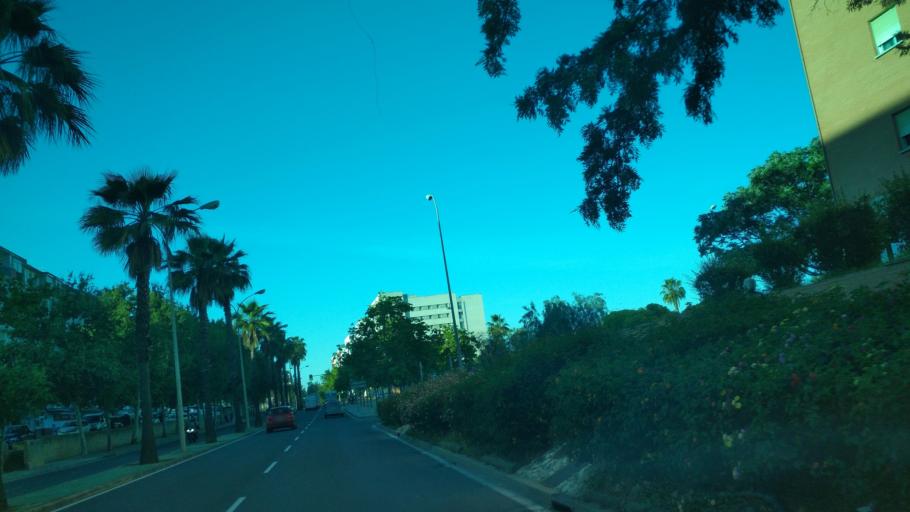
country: ES
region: Andalusia
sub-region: Provincia de Huelva
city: Huelva
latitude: 37.2775
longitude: -6.9486
